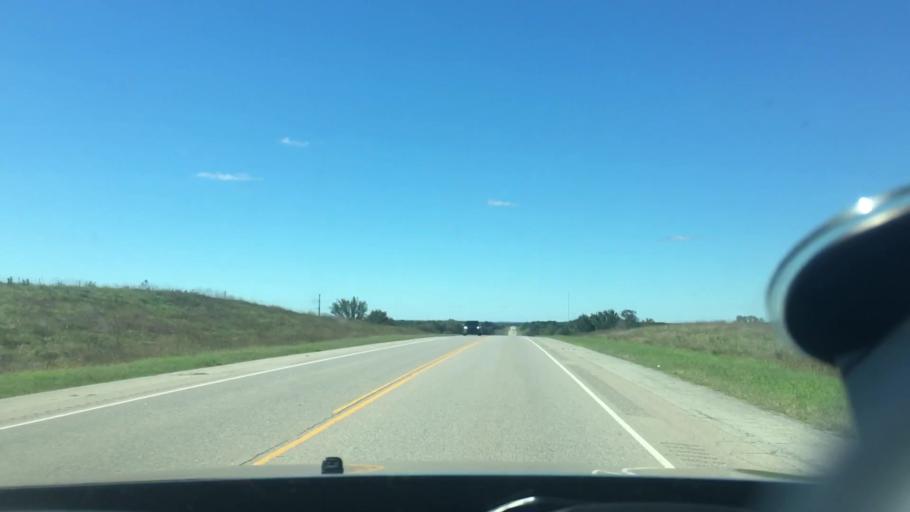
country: US
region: Oklahoma
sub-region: Coal County
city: Coalgate
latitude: 34.6187
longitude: -96.4502
